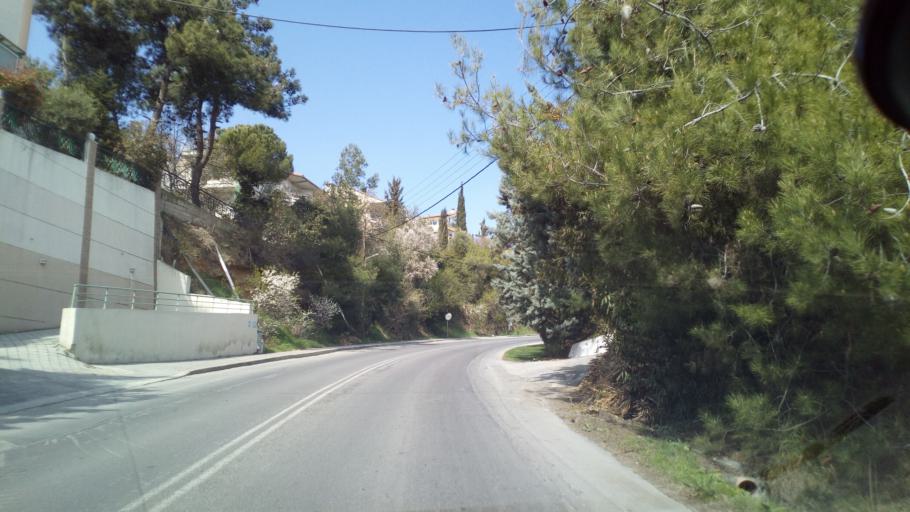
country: GR
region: Central Macedonia
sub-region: Nomos Thessalonikis
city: Panorama
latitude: 40.5769
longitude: 23.0262
